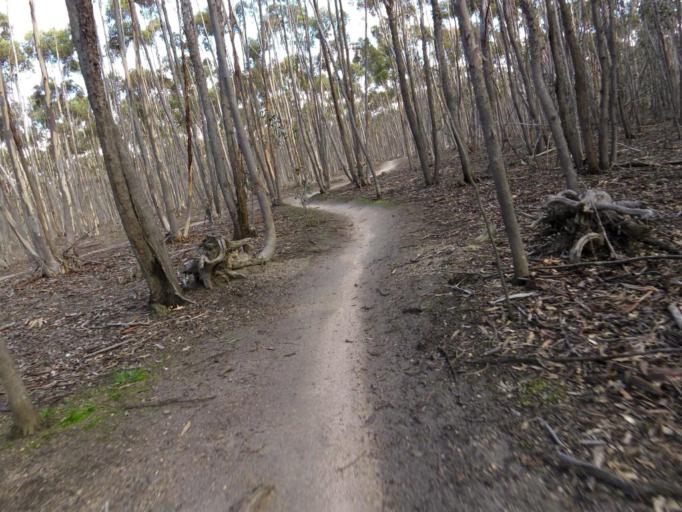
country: AU
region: Victoria
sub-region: Greater Geelong
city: Lara
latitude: -37.9409
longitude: 144.4044
